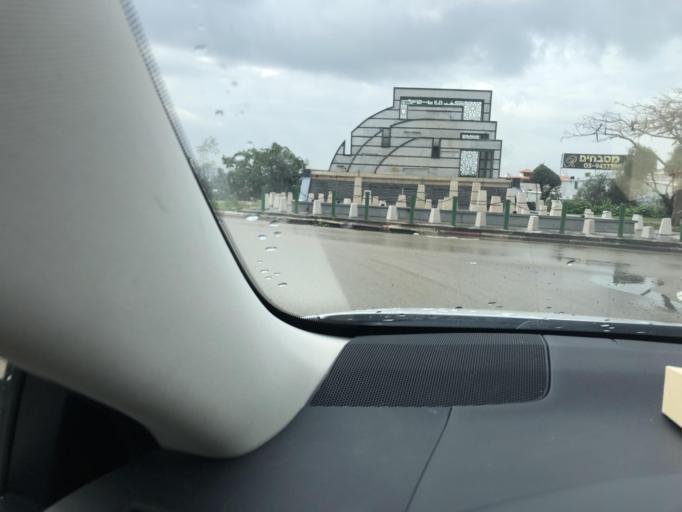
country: IL
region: Central District
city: Kafr Qasim
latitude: 32.1119
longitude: 34.9637
